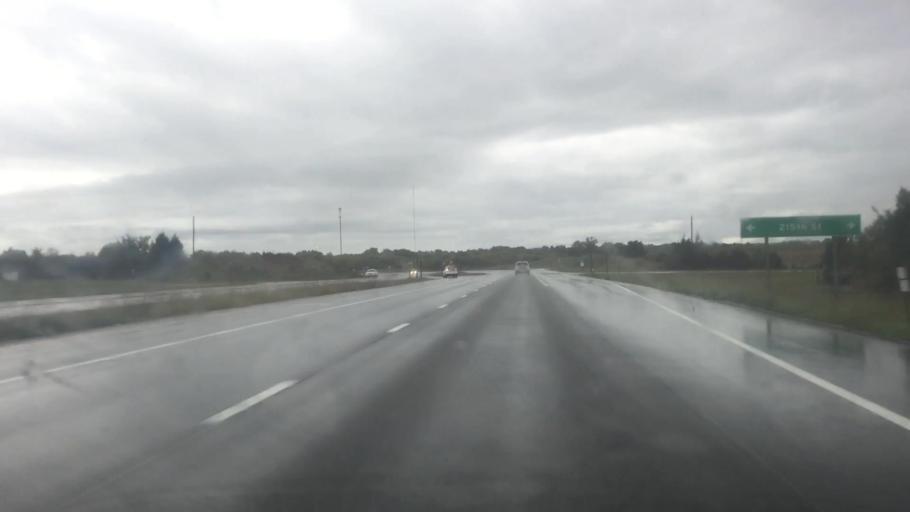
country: US
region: Kansas
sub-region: Johnson County
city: Spring Hill
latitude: 38.7397
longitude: -94.8394
